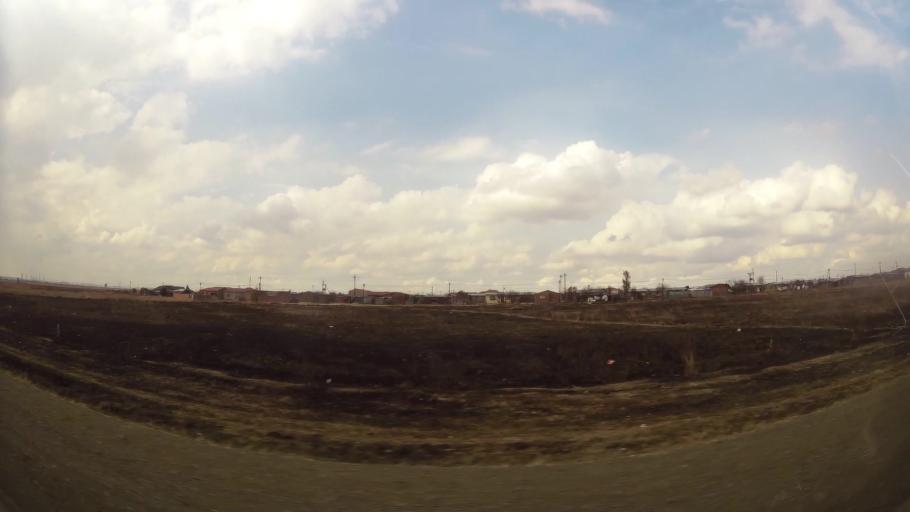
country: ZA
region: Orange Free State
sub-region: Fezile Dabi District Municipality
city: Sasolburg
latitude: -26.8497
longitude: 27.8891
